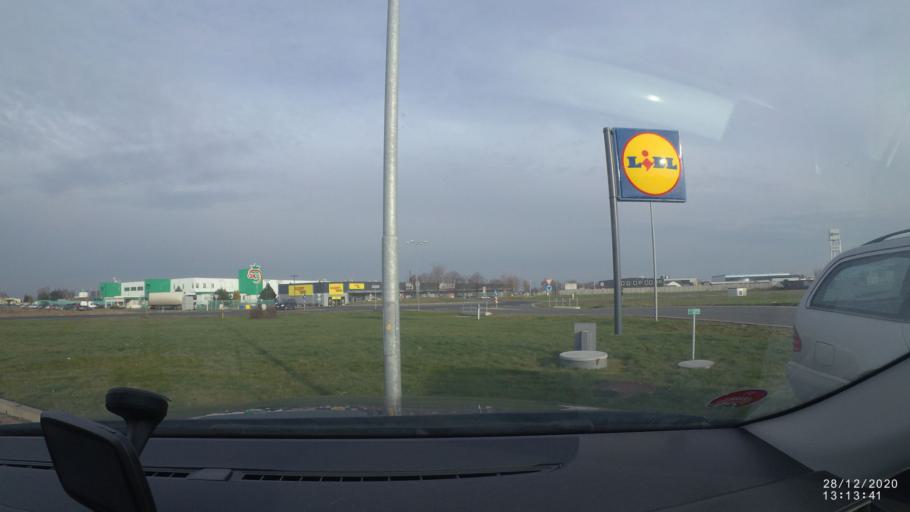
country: CZ
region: Central Bohemia
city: Jirny
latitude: 50.1275
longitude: 14.7103
